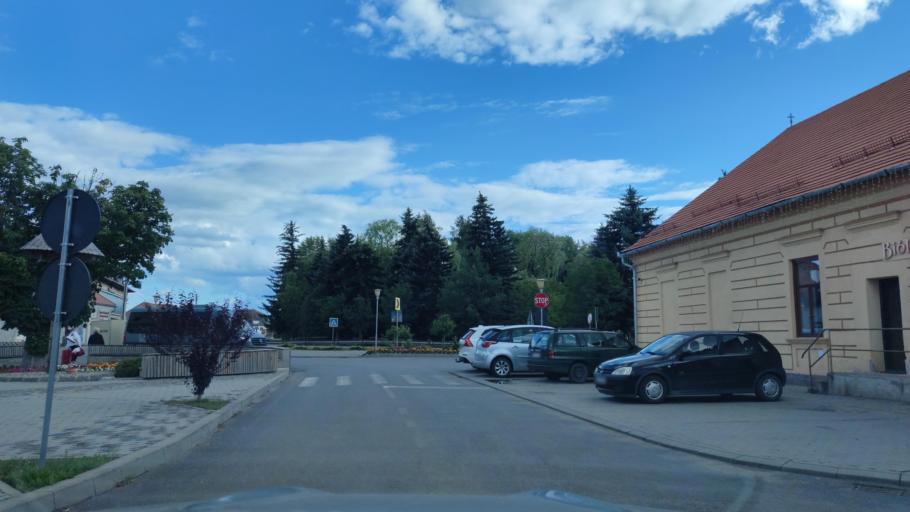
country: RO
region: Harghita
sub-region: Comuna Lazarea
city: Lazarea
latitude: 46.7471
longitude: 25.5329
